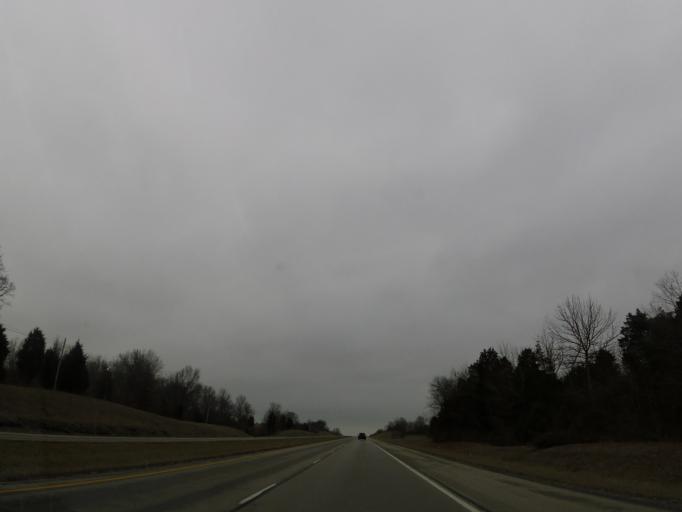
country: US
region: Kentucky
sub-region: Anderson County
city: Lawrenceburg
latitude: 38.0927
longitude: -84.9197
